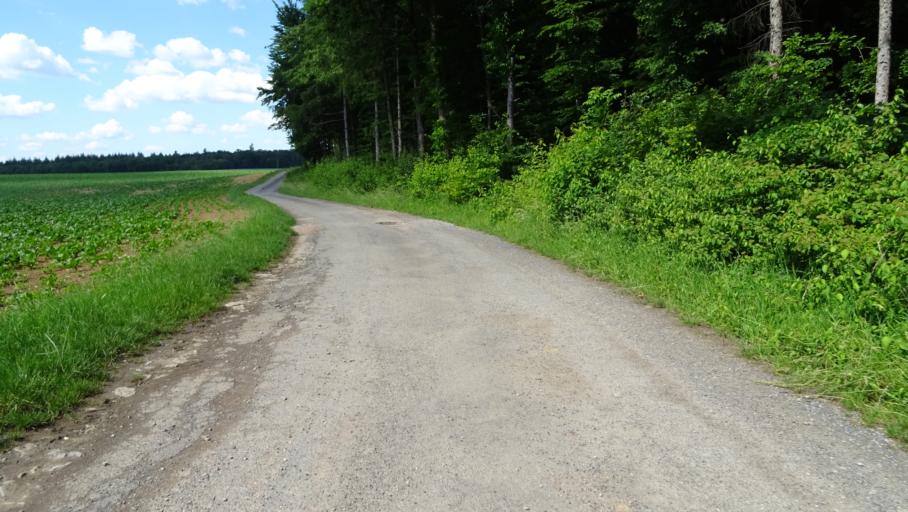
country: DE
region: Baden-Wuerttemberg
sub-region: Karlsruhe Region
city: Adelsheim
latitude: 49.4124
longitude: 9.3660
